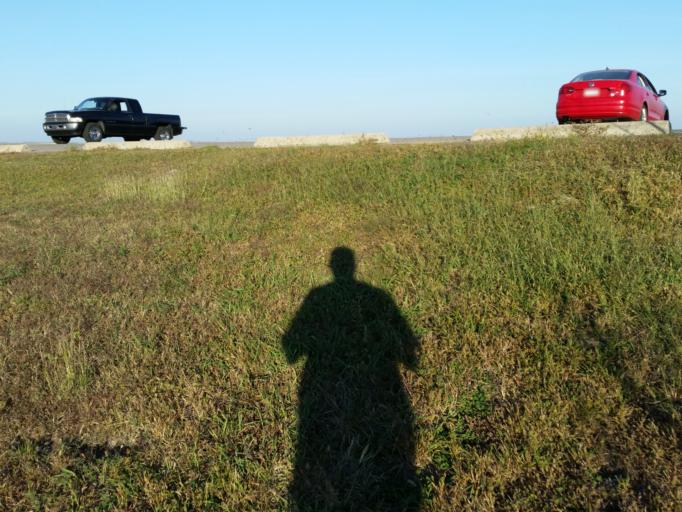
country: US
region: Kansas
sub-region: Riley County
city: Manhattan
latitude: 39.2530
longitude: -96.6058
